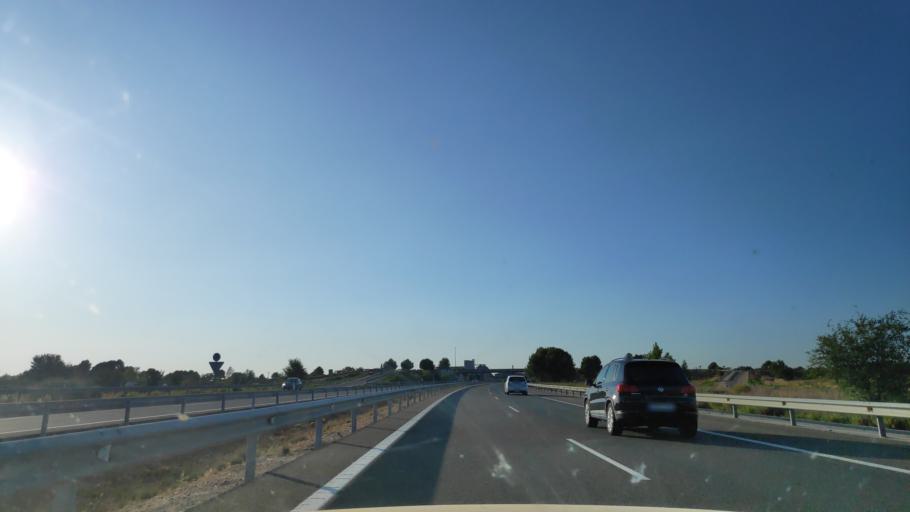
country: ES
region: Castille-La Mancha
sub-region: Provincia de Cuenca
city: Tarancon
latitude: 40.0020
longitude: -3.0248
